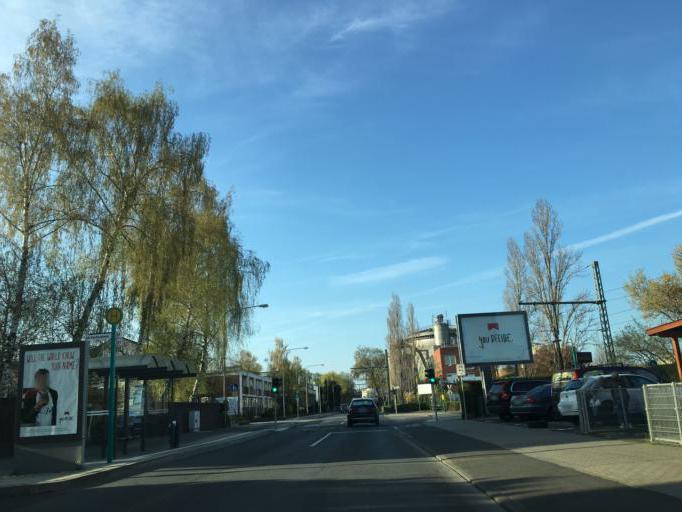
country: DE
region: Hesse
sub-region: Regierungsbezirk Darmstadt
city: Offenbach
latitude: 50.1281
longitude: 8.7675
